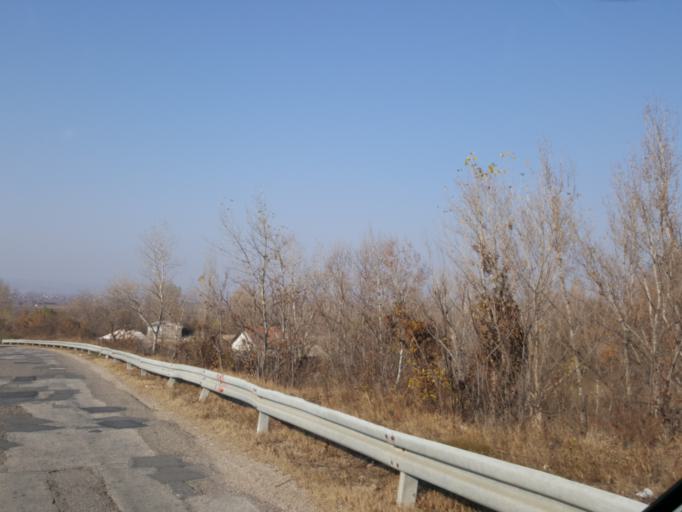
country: RS
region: Central Serbia
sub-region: Borski Okrug
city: Negotin
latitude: 44.2193
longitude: 22.5688
